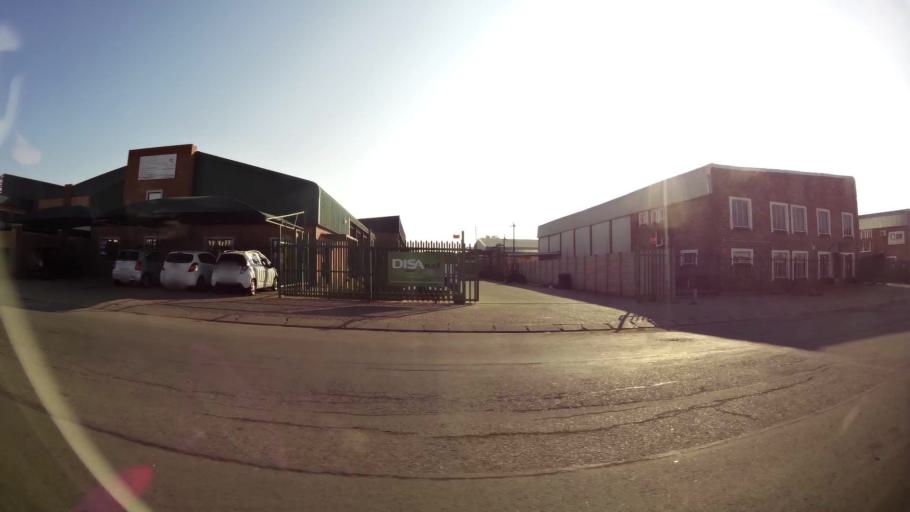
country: ZA
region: Orange Free State
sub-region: Mangaung Metropolitan Municipality
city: Bloemfontein
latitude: -29.1326
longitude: 26.2639
